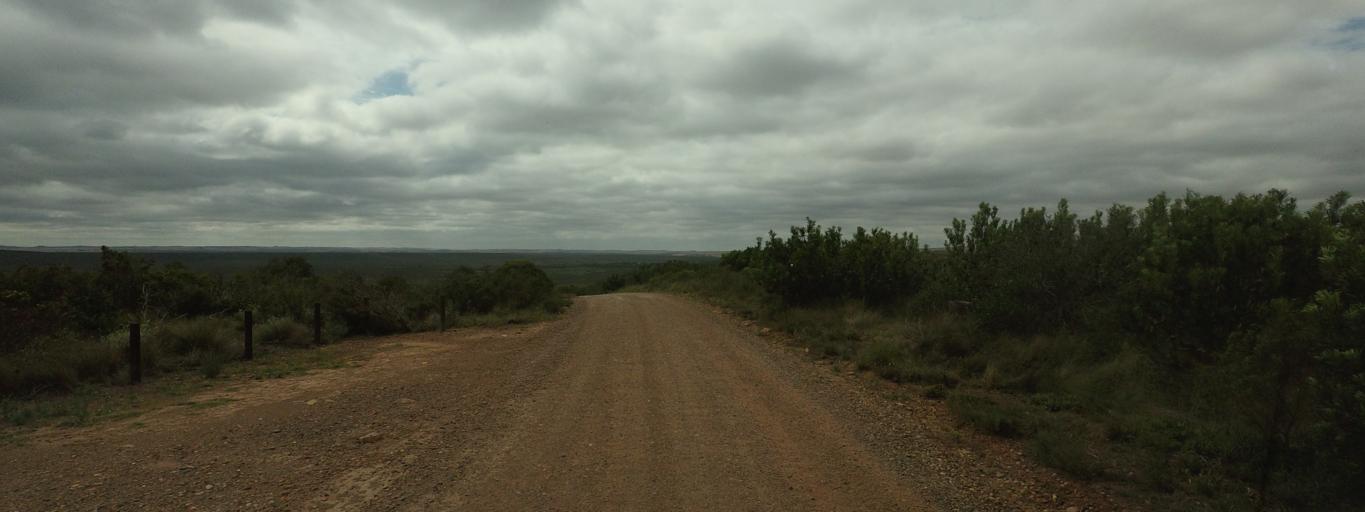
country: ZA
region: Western Cape
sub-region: Overberg District Municipality
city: Swellendam
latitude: -34.0624
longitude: 20.4341
